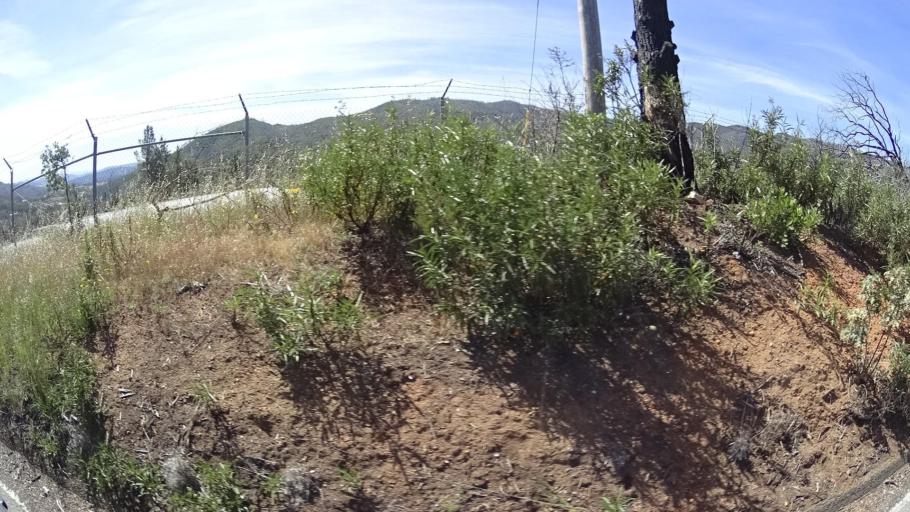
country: US
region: California
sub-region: Lake County
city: Cobb
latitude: 38.7803
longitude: -122.6894
